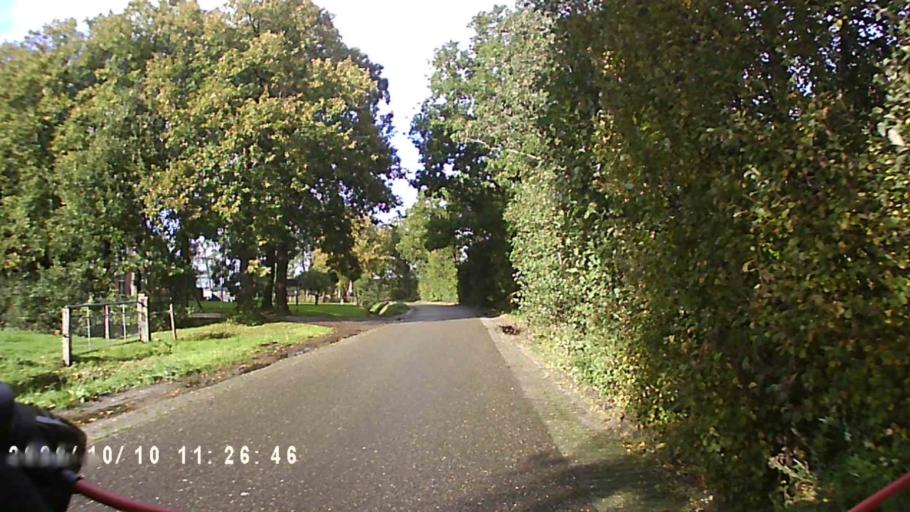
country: NL
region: Friesland
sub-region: Gemeente Smallingerland
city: Drachtstercompagnie
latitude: 53.0878
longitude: 6.1626
